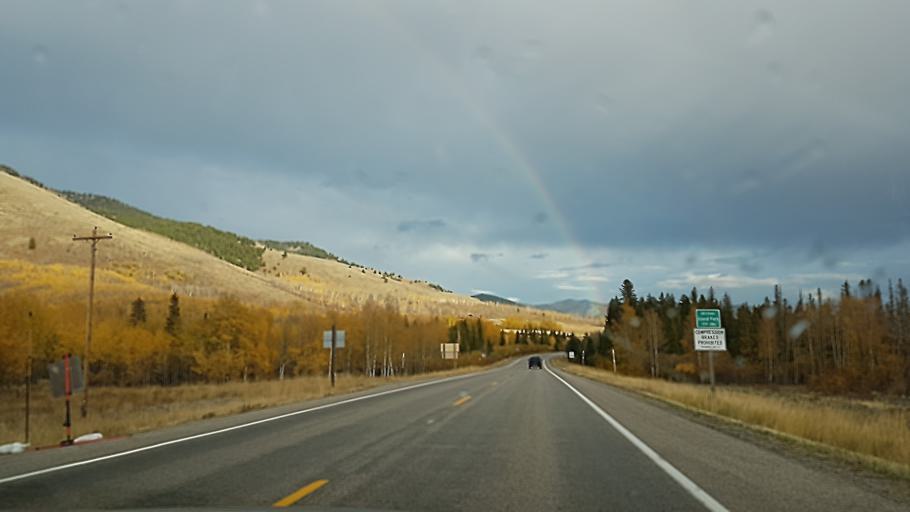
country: US
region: Montana
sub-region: Gallatin County
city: West Yellowstone
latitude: 44.6734
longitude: -111.4085
